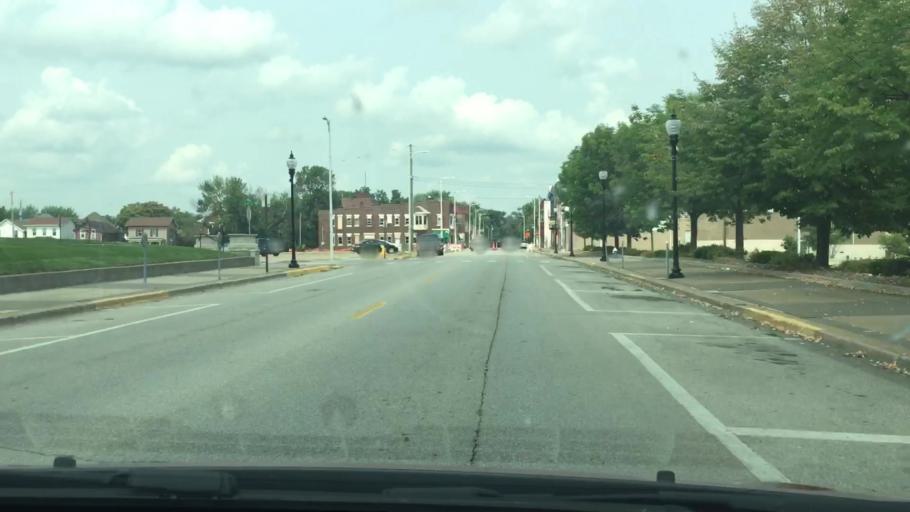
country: US
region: Iowa
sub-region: Muscatine County
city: Muscatine
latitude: 41.4249
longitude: -91.0426
